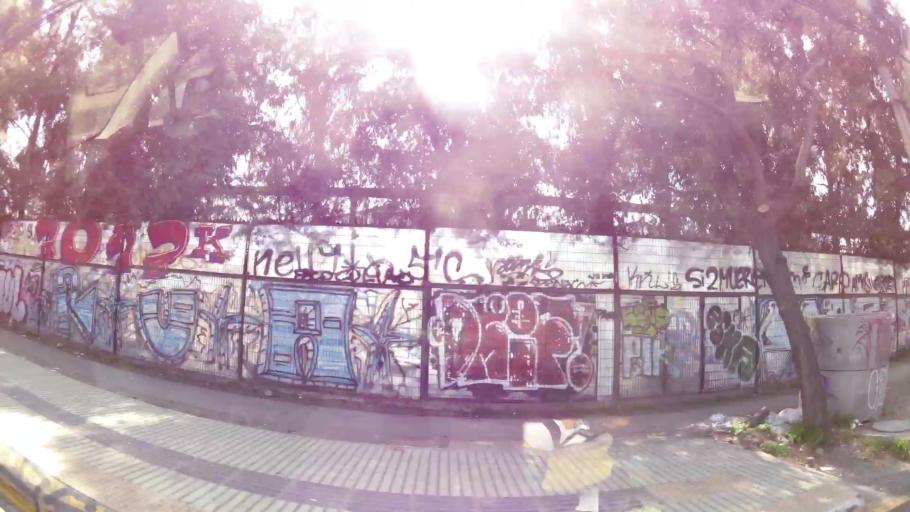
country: CL
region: Santiago Metropolitan
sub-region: Provincia de Santiago
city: Villa Presidente Frei, Nunoa, Santiago, Chile
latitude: -33.4697
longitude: -70.5511
